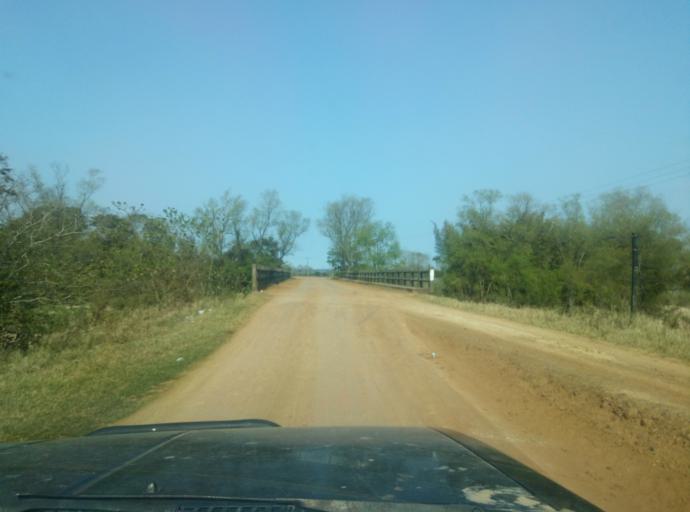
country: PY
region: Caaguazu
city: Coronel Oviedo
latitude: -25.3409
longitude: -56.3159
